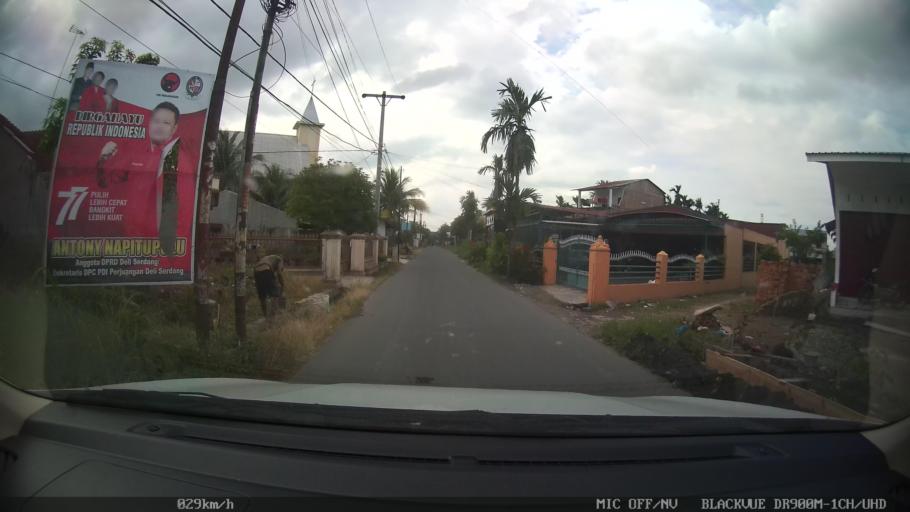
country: ID
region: North Sumatra
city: Sunggal
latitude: 3.6161
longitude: 98.6258
